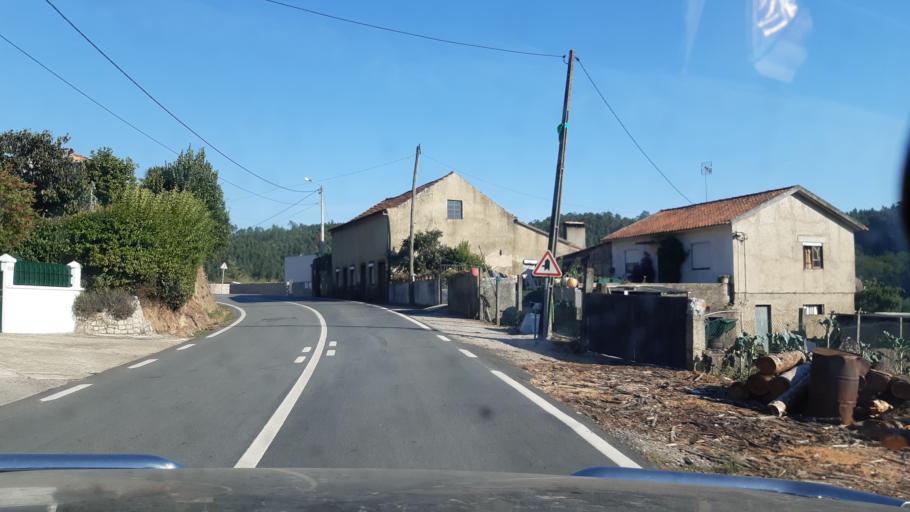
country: PT
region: Aveiro
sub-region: Agueda
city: Agueda
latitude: 40.5641
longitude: -8.4125
